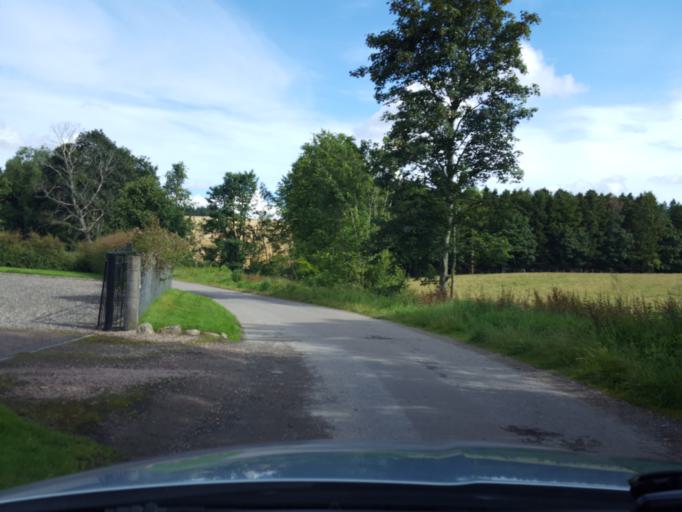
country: GB
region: Scotland
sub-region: Moray
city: Rothes
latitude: 57.4746
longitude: -3.1972
